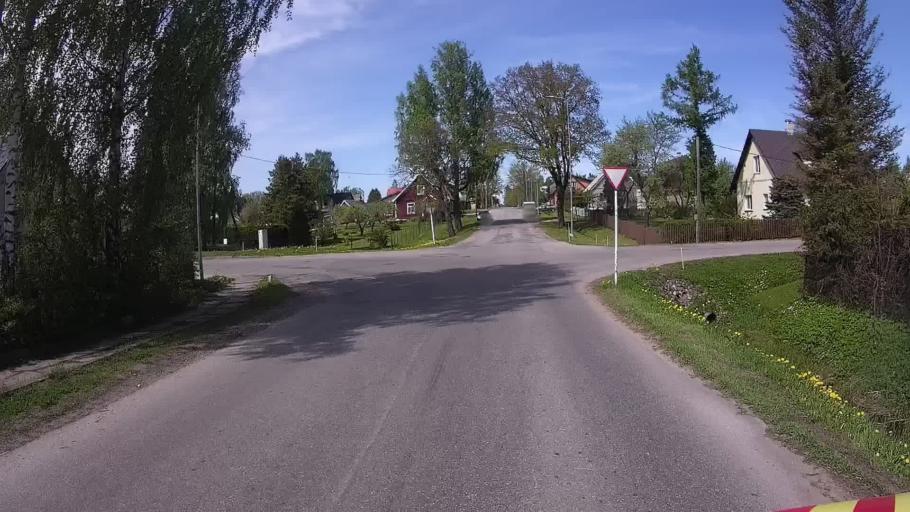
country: EE
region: Valgamaa
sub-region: Valga linn
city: Valga
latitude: 57.7787
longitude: 26.0637
